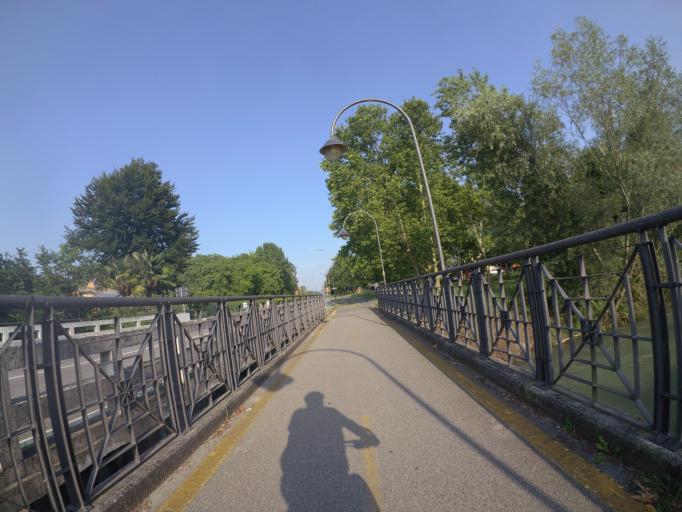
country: IT
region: Friuli Venezia Giulia
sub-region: Provincia di Udine
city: Codroipo
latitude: 45.9587
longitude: 12.9946
